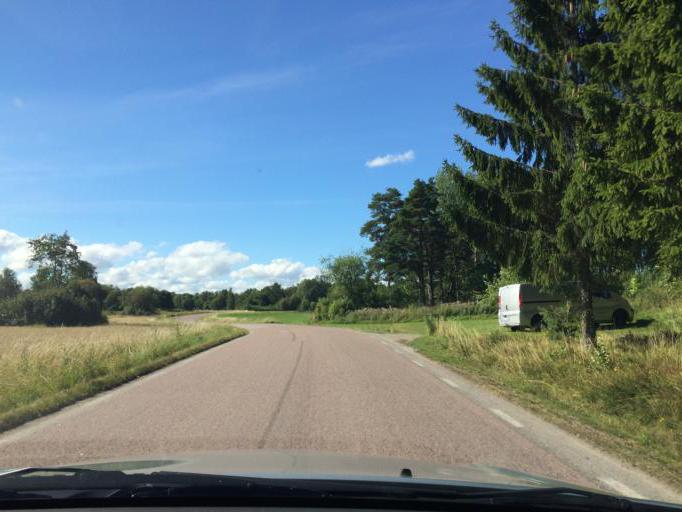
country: SE
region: Soedermanland
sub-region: Eskilstuna Kommun
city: Torshalla
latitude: 59.5306
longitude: 16.4434
